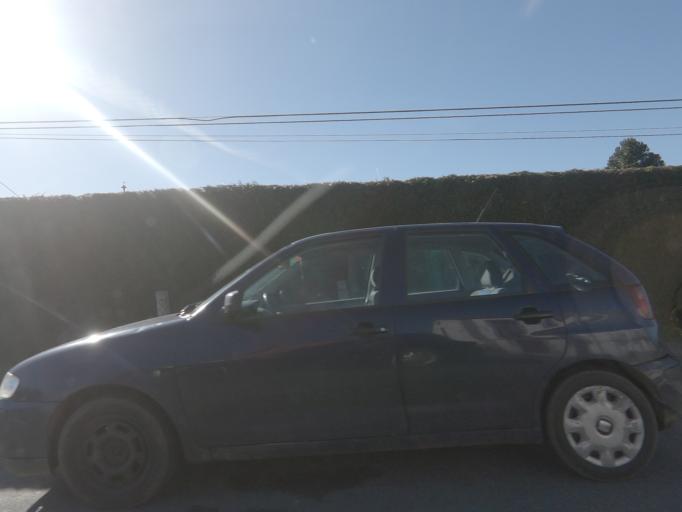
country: ES
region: Galicia
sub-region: Provincia de Pontevedra
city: Silleda
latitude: 42.6837
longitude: -8.1864
